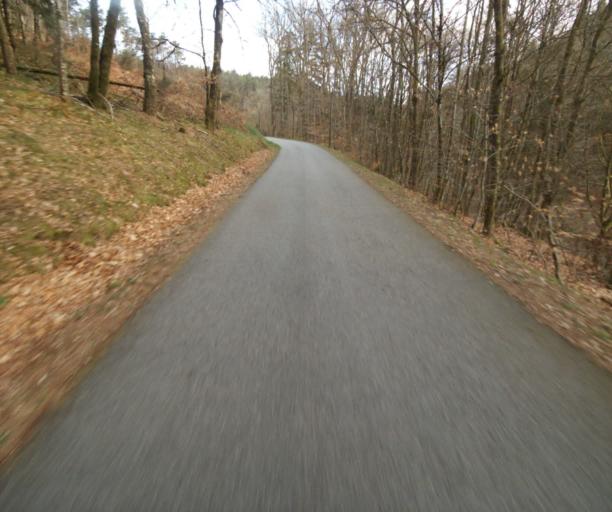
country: FR
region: Limousin
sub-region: Departement de la Correze
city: Correze
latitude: 45.3814
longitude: 1.8778
